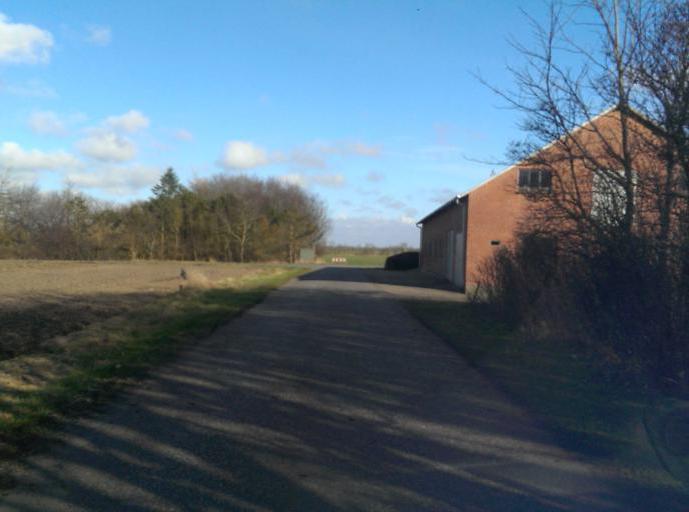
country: DK
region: South Denmark
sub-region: Esbjerg Kommune
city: Bramming
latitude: 55.4519
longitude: 8.7513
